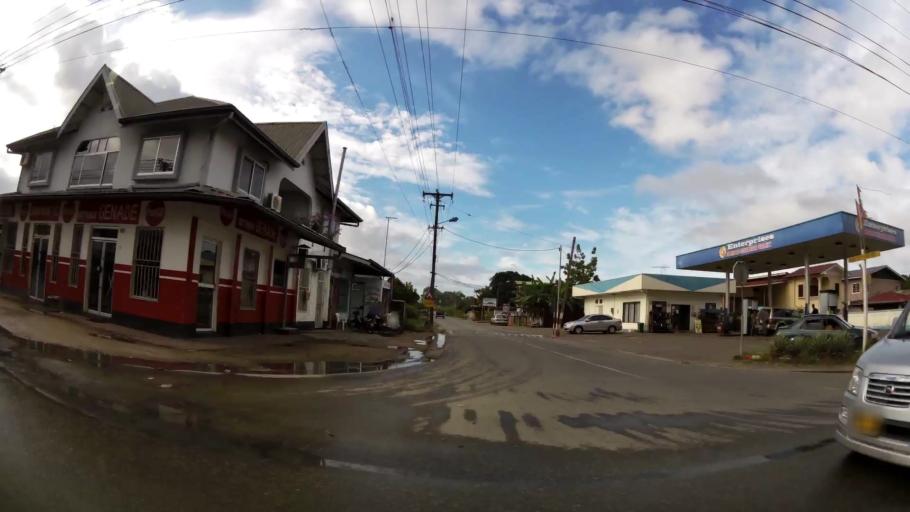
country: SR
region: Paramaribo
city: Paramaribo
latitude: 5.8457
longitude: -55.2267
